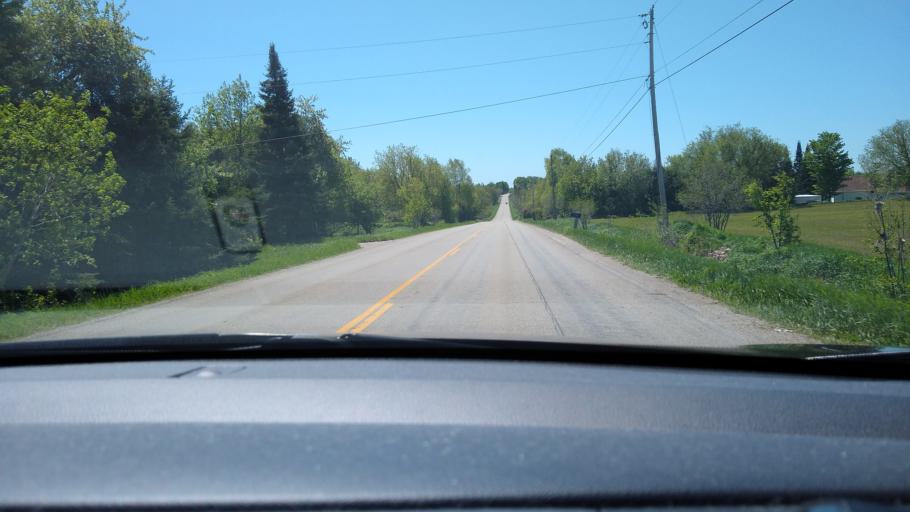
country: US
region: Michigan
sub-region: Delta County
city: Escanaba
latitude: 45.8352
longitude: -87.1837
